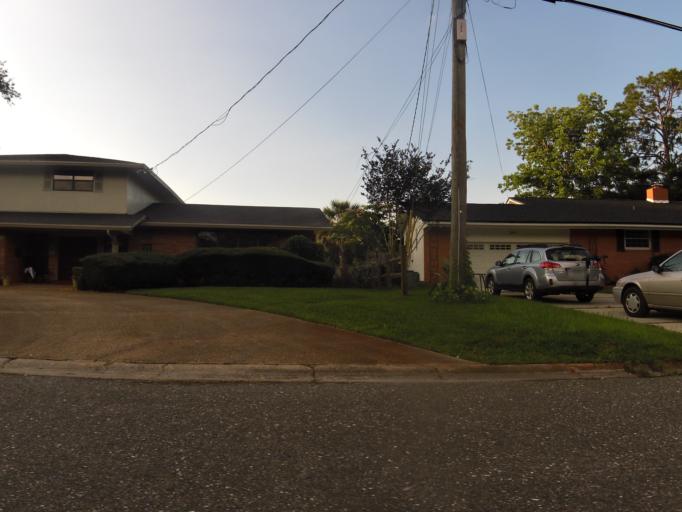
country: US
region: Florida
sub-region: Clay County
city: Orange Park
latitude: 30.2249
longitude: -81.6138
